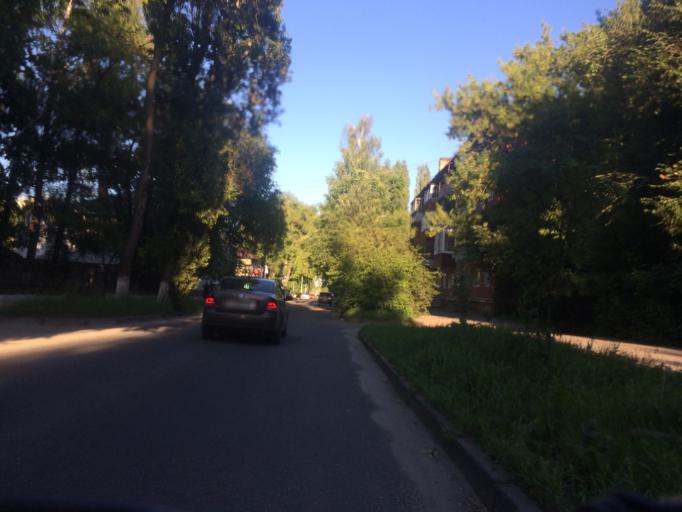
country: RU
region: Kursk
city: Kursk
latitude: 51.6723
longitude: 36.1499
